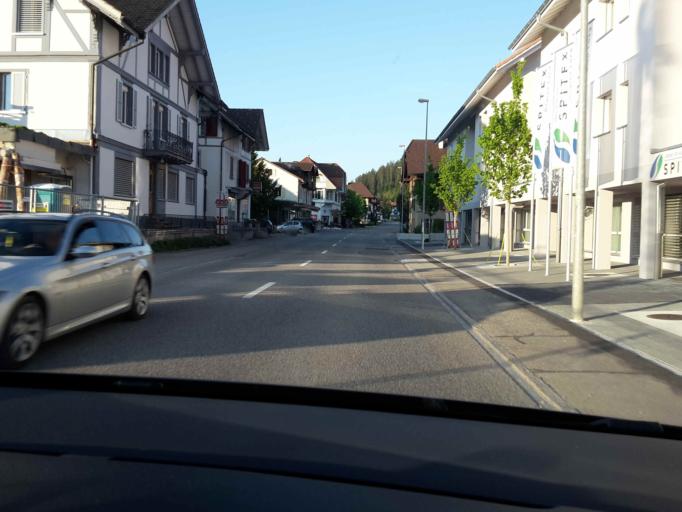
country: CH
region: Bern
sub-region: Emmental District
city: Lutzelfluh
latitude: 47.0175
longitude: 7.6587
